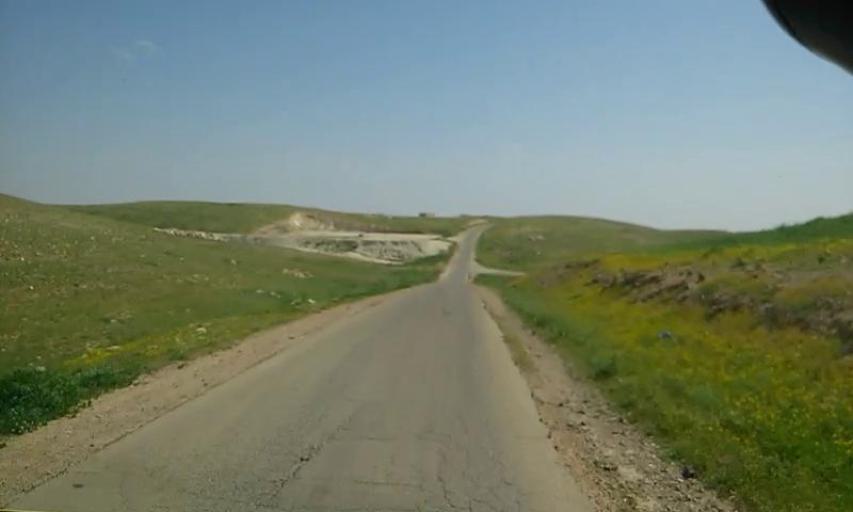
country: PS
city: `Arab ar Rashaydah
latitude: 31.5476
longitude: 35.2563
